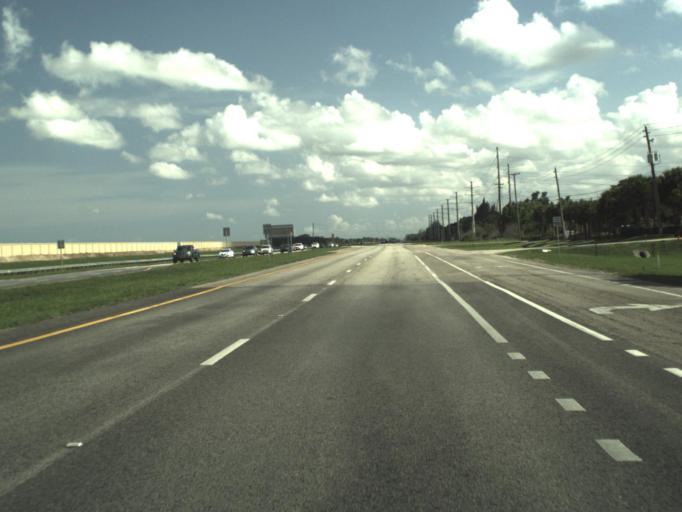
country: US
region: Florida
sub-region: Palm Beach County
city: Villages of Oriole
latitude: 26.4372
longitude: -80.2046
